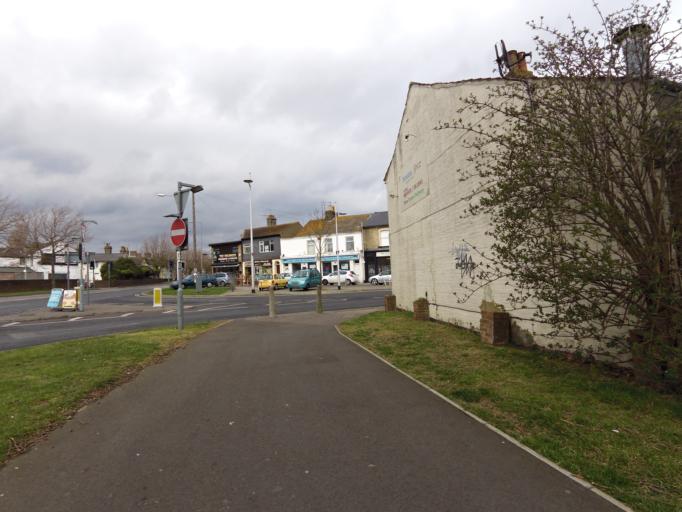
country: GB
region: England
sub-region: Suffolk
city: Lowestoft
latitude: 52.4752
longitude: 1.7492
